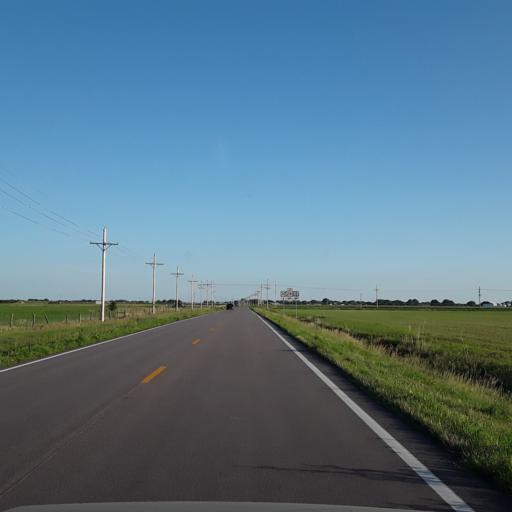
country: US
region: Nebraska
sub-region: Hall County
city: Grand Island
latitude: 40.9632
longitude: -98.3206
